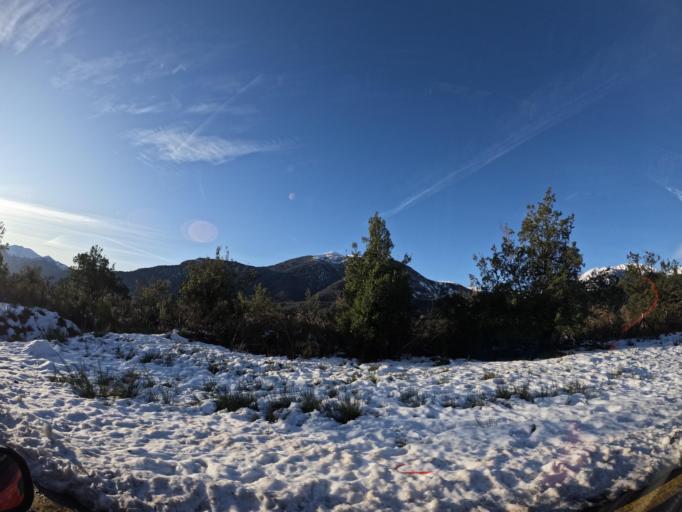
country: CL
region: Biobio
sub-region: Provincia de Nuble
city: Coihueco
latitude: -37.3670
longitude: -71.5022
